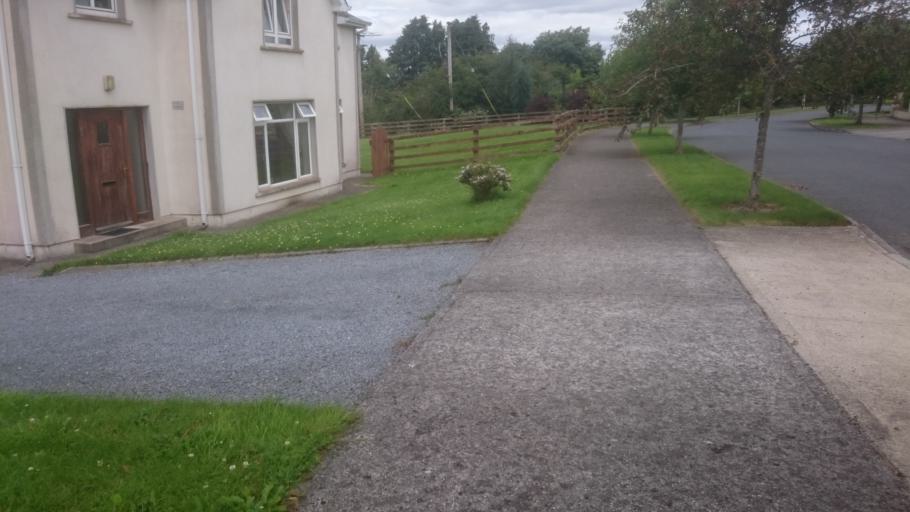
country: IE
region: Leinster
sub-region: Kilkenny
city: Callan
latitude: 52.5377
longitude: -7.2734
